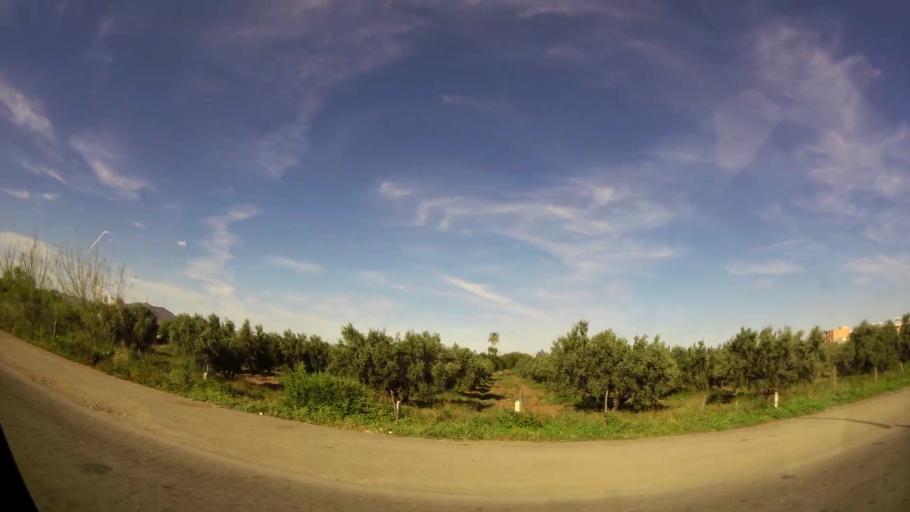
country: MA
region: Marrakech-Tensift-Al Haouz
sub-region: Marrakech
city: Marrakesh
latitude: 31.6825
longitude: -8.0502
